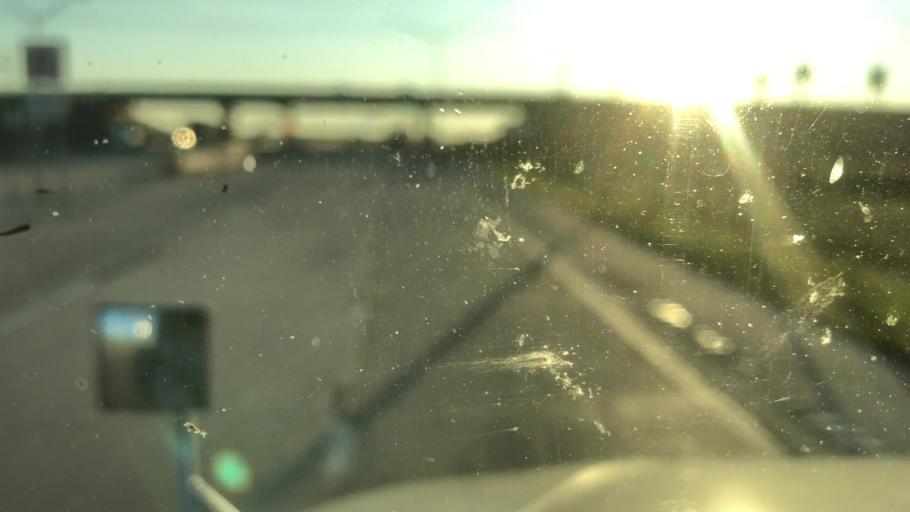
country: US
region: Oklahoma
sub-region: Noble County
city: Perry
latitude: 36.3837
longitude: -97.0664
